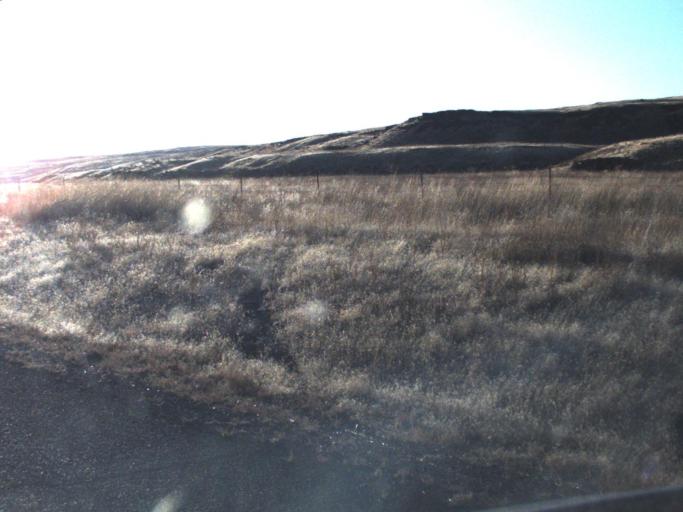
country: US
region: Washington
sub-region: Franklin County
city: Connell
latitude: 46.6833
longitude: -118.4431
